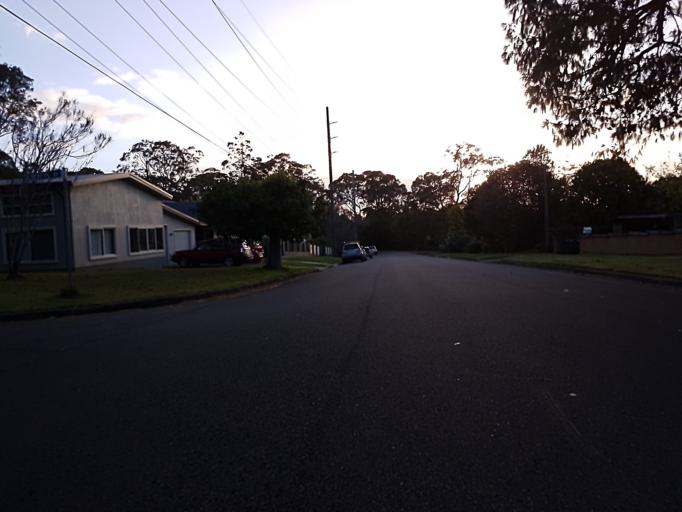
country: AU
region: New South Wales
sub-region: Warringah
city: Killarney Heights
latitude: -33.7591
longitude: 151.2302
